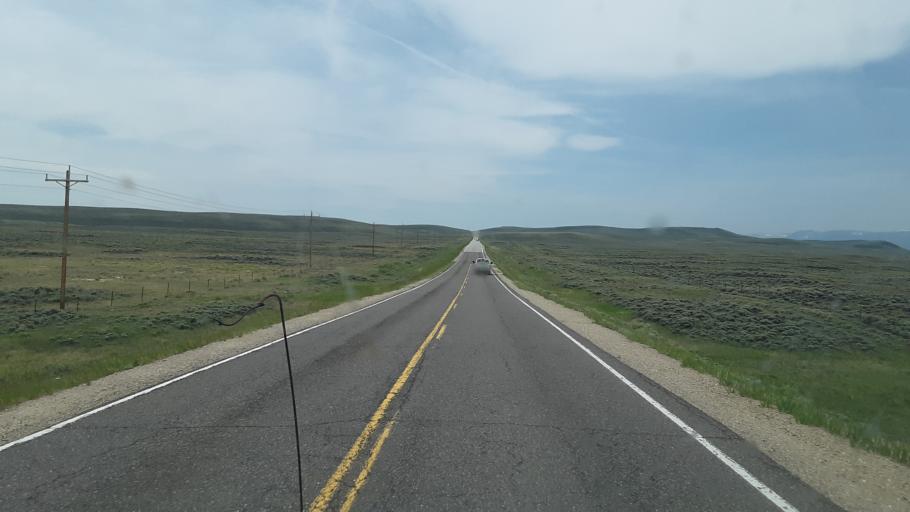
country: US
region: Colorado
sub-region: Jackson County
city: Walden
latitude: 40.6804
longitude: -106.3693
